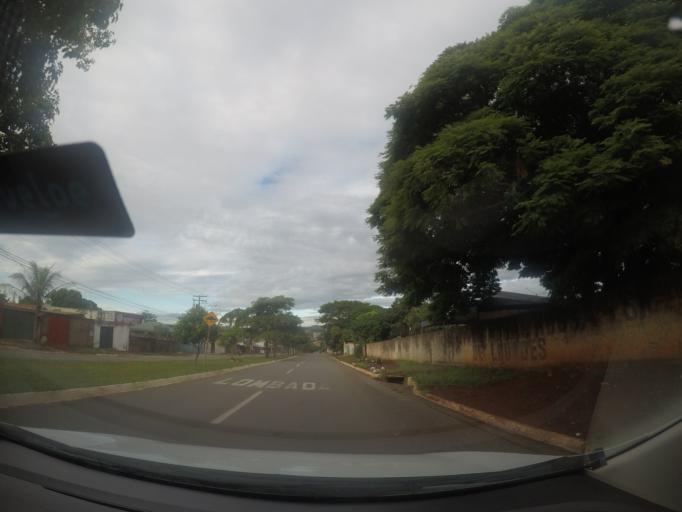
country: BR
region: Goias
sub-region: Goiania
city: Goiania
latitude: -16.6067
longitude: -49.3375
